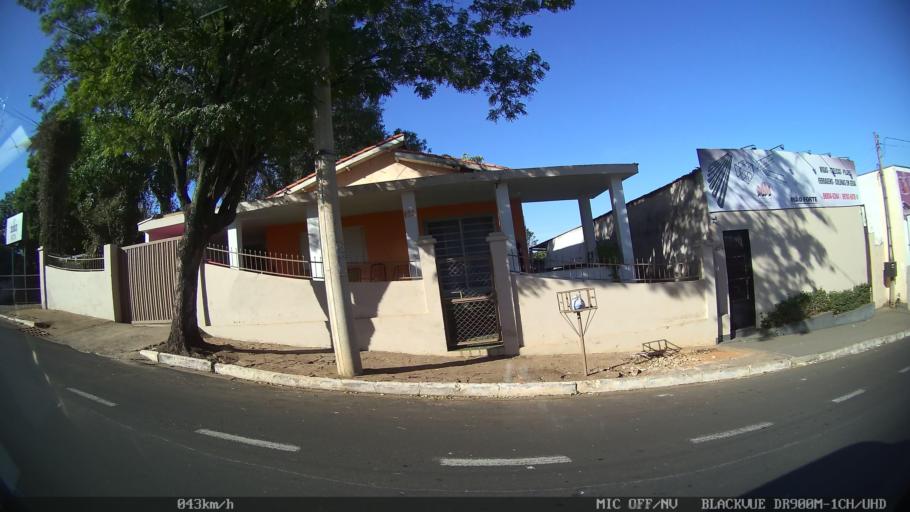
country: BR
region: Sao Paulo
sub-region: Olimpia
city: Olimpia
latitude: -20.7379
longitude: -48.9037
